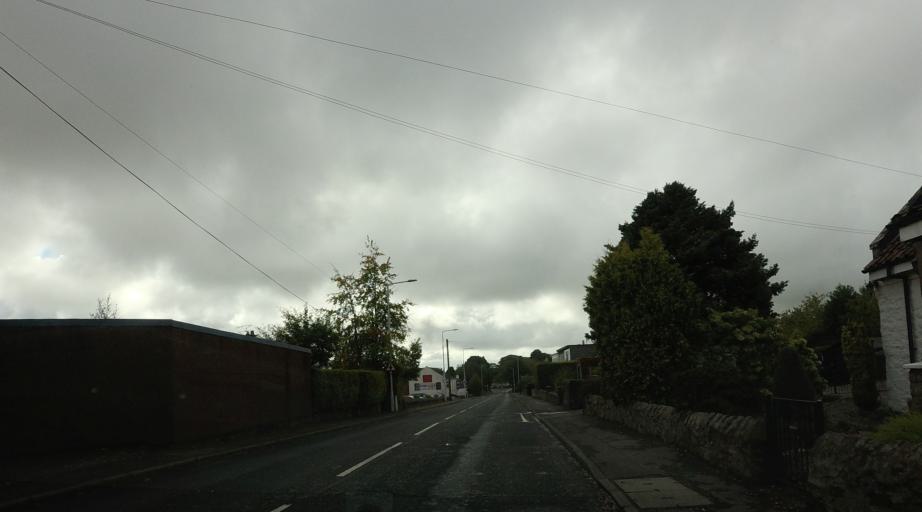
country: GB
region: Scotland
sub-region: Fife
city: Balmullo
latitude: 56.3774
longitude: -2.9258
